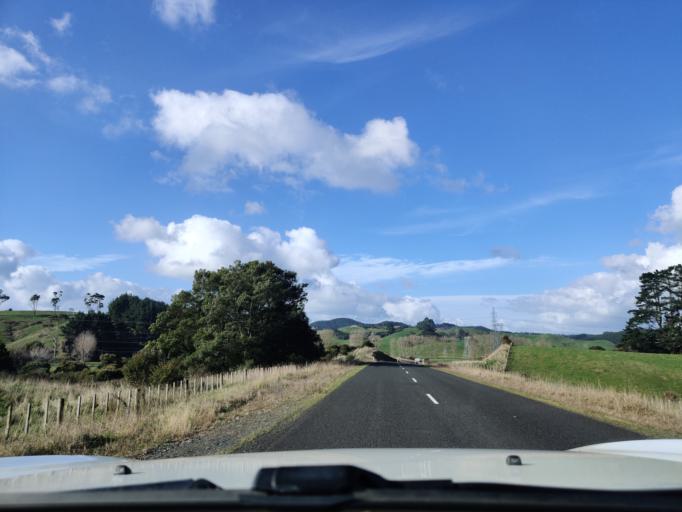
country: NZ
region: Waikato
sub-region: Waikato District
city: Te Kauwhata
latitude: -37.2830
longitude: 175.2049
